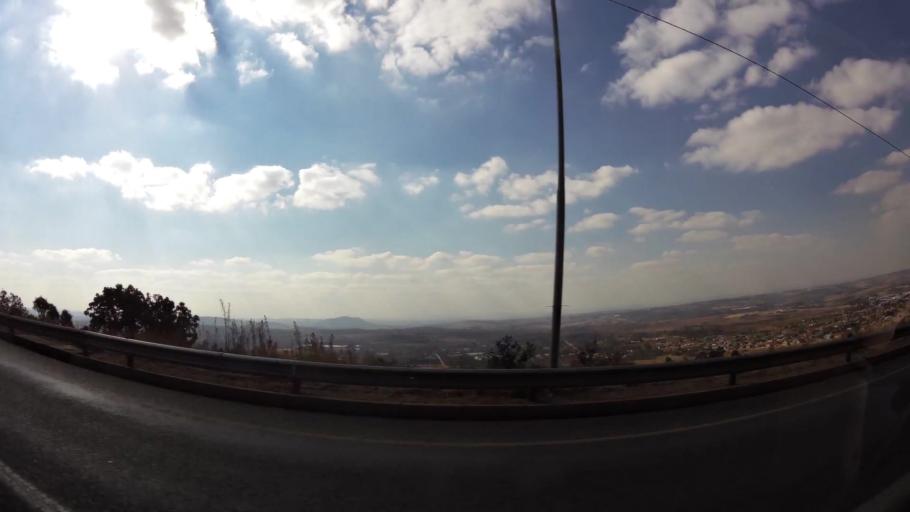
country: ZA
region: Gauteng
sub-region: West Rand District Municipality
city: Muldersdriseloop
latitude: -26.0643
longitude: 27.8130
